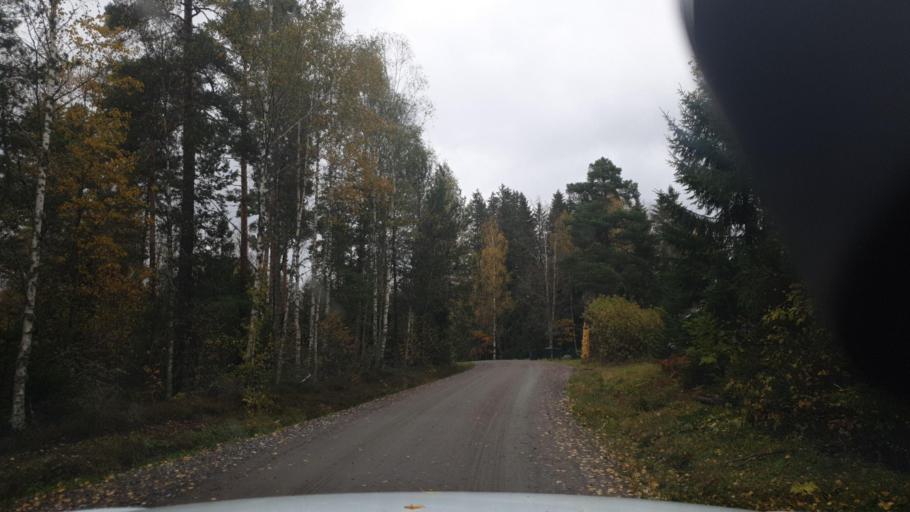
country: SE
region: Vaermland
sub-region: Karlstads Kommun
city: Edsvalla
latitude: 59.4892
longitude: 13.1650
